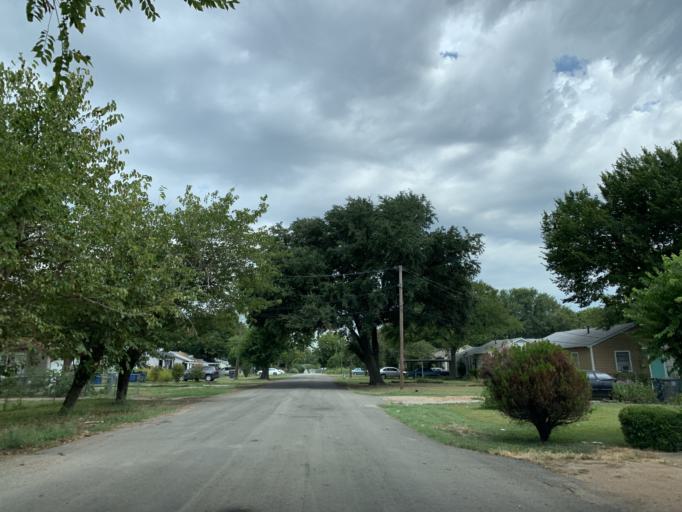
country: US
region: Texas
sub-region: Dallas County
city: DeSoto
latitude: 32.6671
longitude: -96.8267
